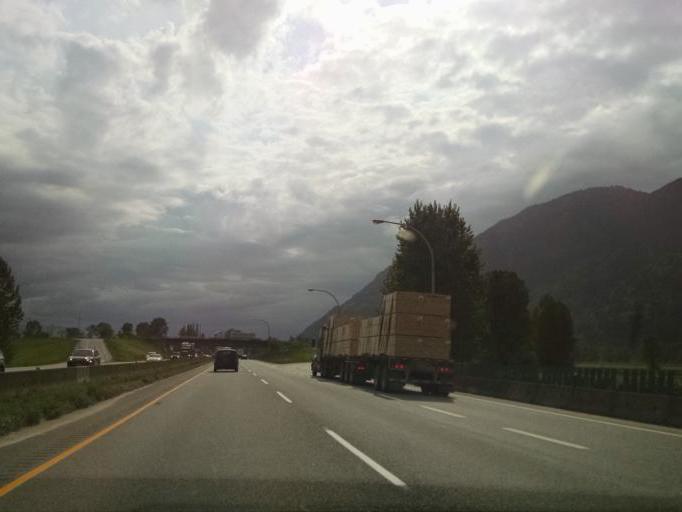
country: CA
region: British Columbia
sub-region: Fraser Valley Regional District
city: Chilliwack
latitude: 49.1319
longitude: -122.0789
